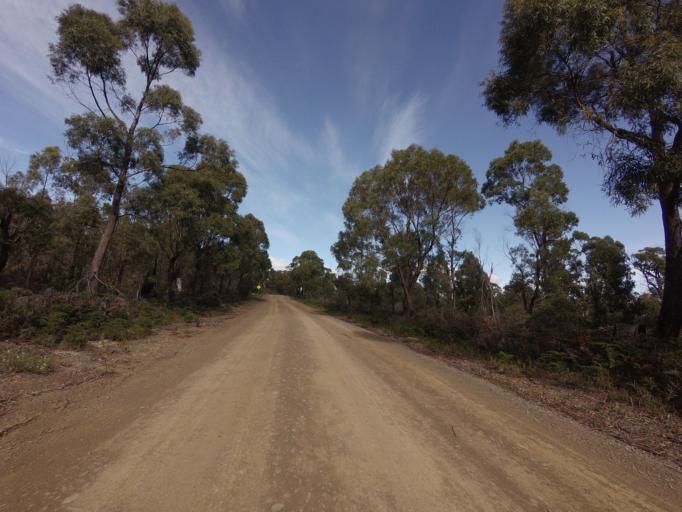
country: AU
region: Tasmania
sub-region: Clarence
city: Sandford
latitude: -42.9806
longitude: 147.7138
